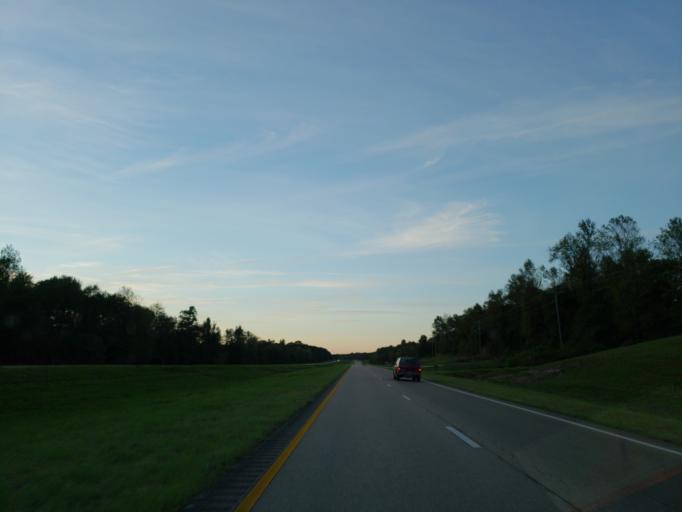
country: US
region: Mississippi
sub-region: Wayne County
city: Belmont
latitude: 31.5916
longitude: -88.5500
